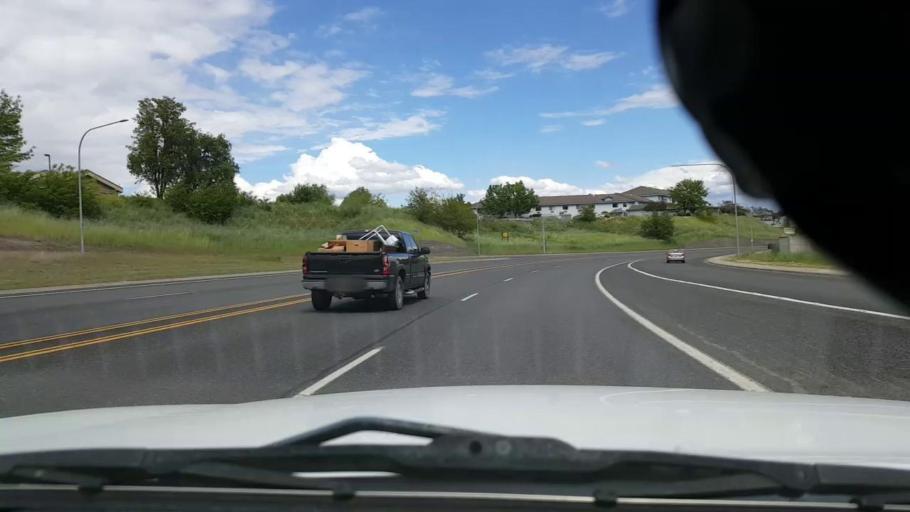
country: US
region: Washington
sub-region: Asotin County
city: West Clarkston-Highland
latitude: 46.4015
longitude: -117.0581
